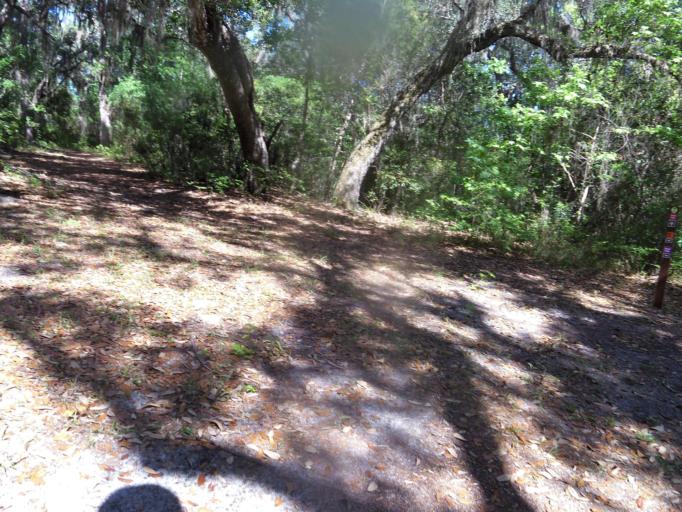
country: US
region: Florida
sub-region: Duval County
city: Atlantic Beach
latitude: 30.4479
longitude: -81.4830
